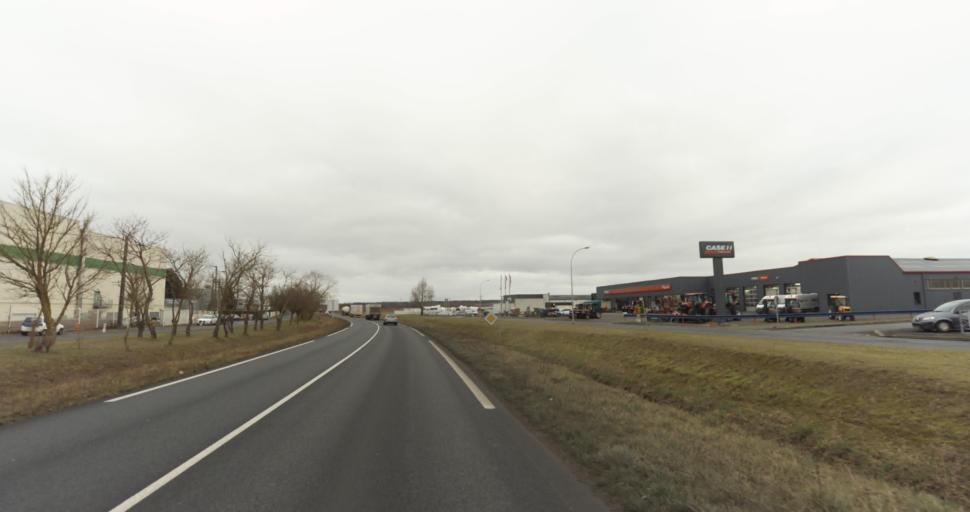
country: FR
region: Pays de la Loire
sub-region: Departement de Maine-et-Loire
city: Doue-la-Fontaine
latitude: 47.1842
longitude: -0.2451
